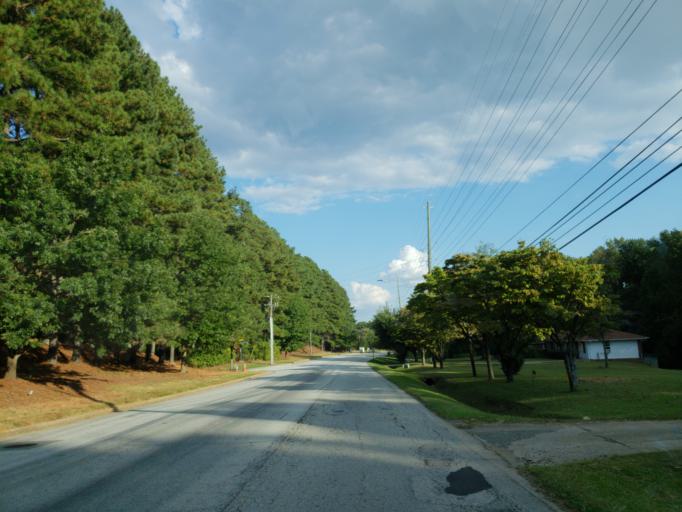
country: US
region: Georgia
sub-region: Cobb County
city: Mableton
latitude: 33.7634
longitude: -84.5933
